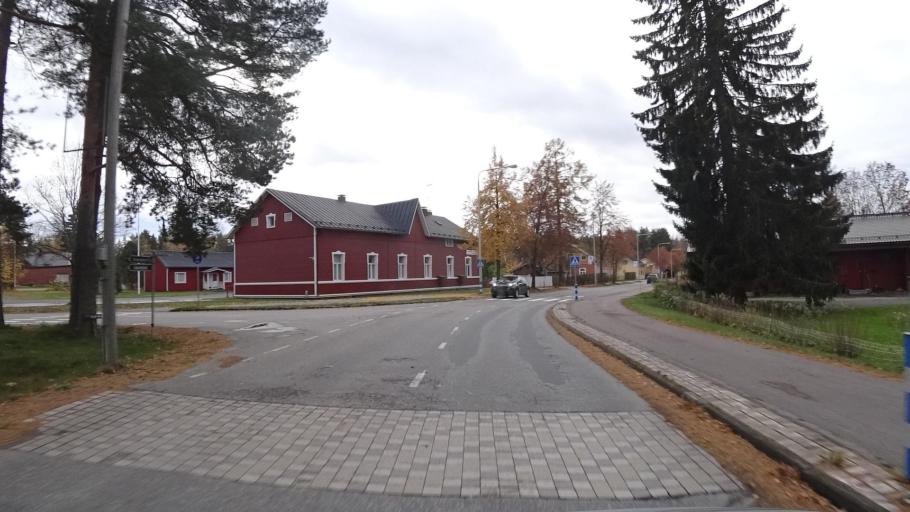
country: FI
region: Central Finland
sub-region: Joutsa
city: Joutsa
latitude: 61.7454
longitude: 26.1203
